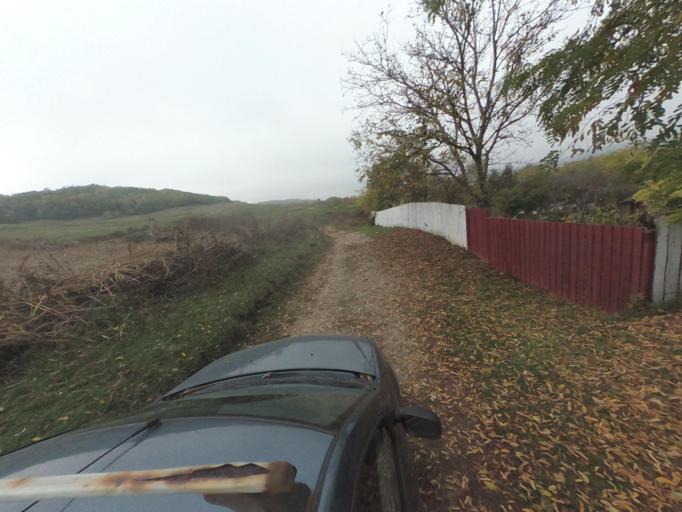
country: RO
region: Vaslui
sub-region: Comuna Bacesti
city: Bacesti
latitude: 46.8303
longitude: 27.2348
